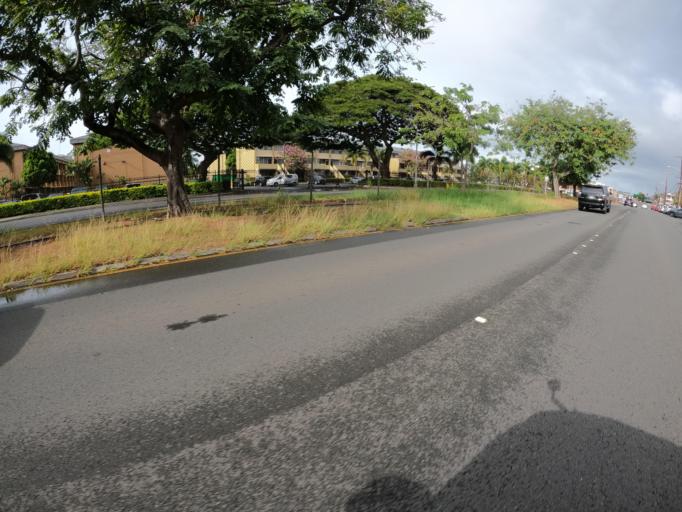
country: US
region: Hawaii
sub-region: Honolulu County
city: Honolulu
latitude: 21.3189
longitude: -157.8612
